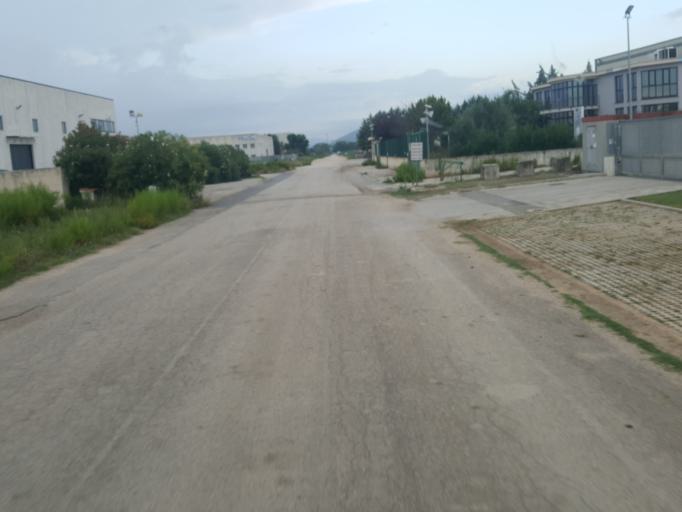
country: IT
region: Campania
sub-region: Provincia di Caserta
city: Pignataro Maggiore
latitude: 41.1757
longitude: 14.1437
